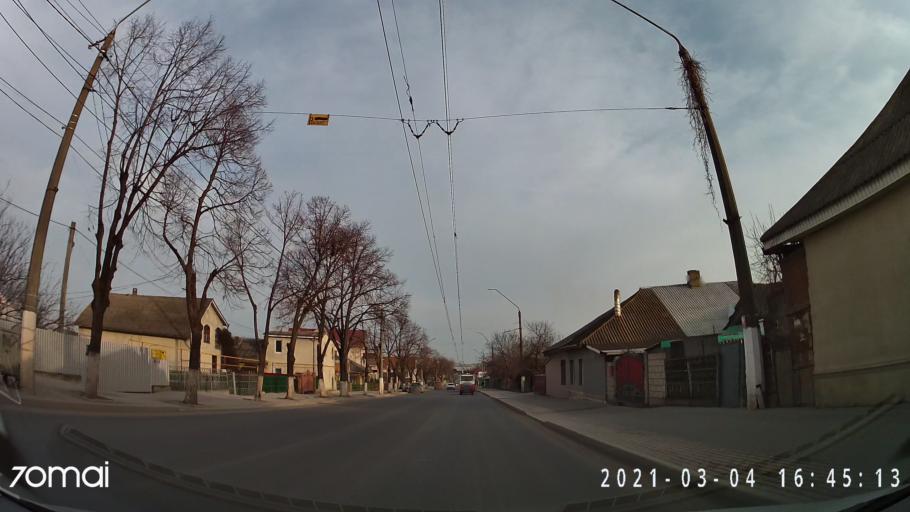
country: MD
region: Balti
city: Balti
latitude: 47.7657
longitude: 27.9058
